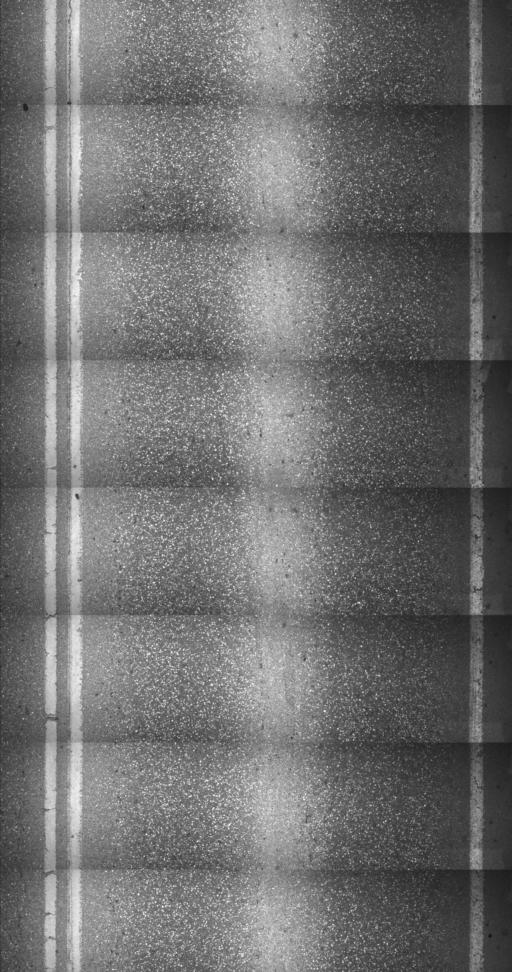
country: US
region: Vermont
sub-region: Chittenden County
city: Hinesburg
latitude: 44.3384
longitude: -73.1147
